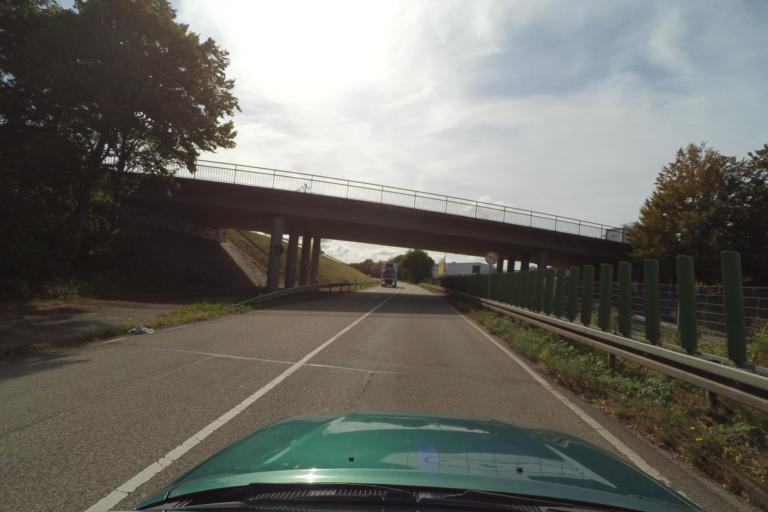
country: DE
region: Baden-Wuerttemberg
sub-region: Freiburg Region
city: Offenburg
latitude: 48.4787
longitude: 7.9241
